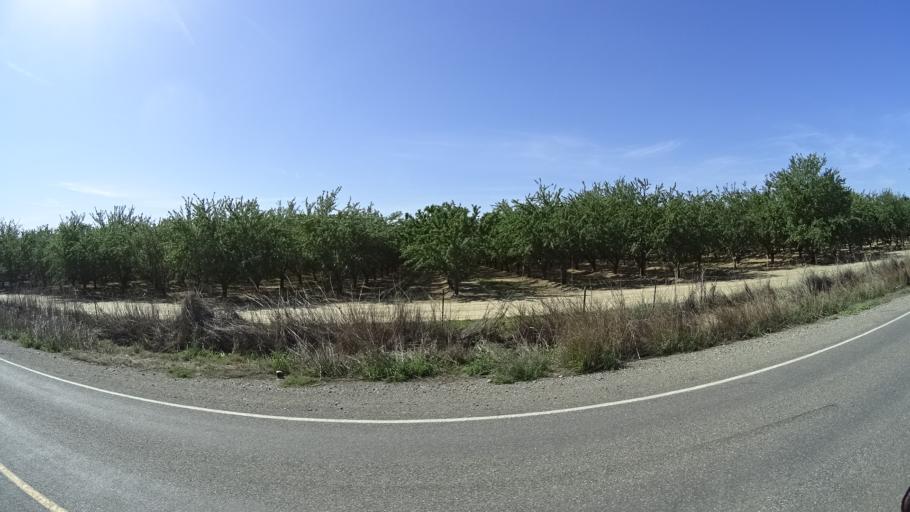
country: US
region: California
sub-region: Glenn County
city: Willows
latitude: 39.6241
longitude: -122.1887
